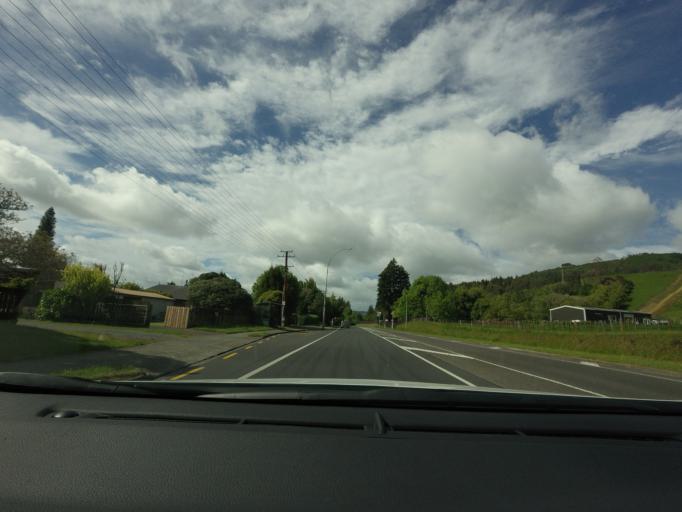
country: NZ
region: Bay of Plenty
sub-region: Rotorua District
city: Rotorua
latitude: -38.1044
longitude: 176.2217
